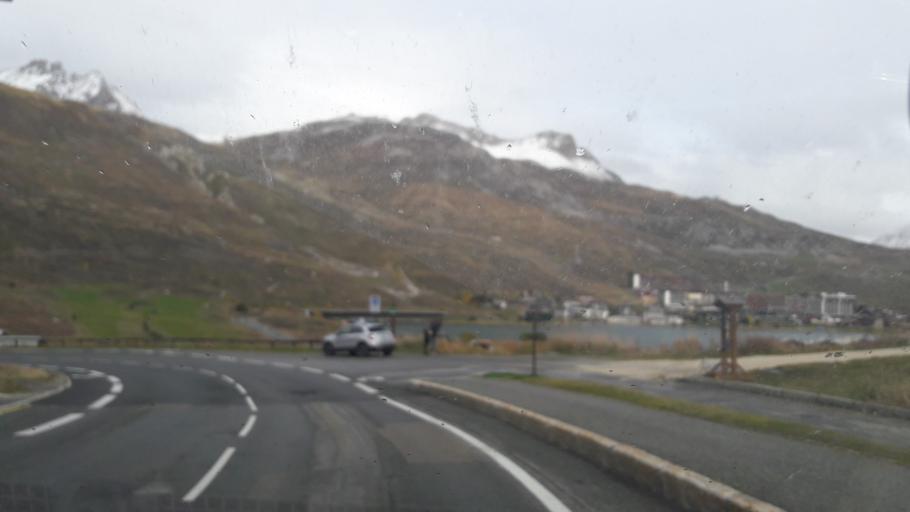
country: FR
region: Rhone-Alpes
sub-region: Departement de la Savoie
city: Tignes
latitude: 45.4590
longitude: 6.9020
